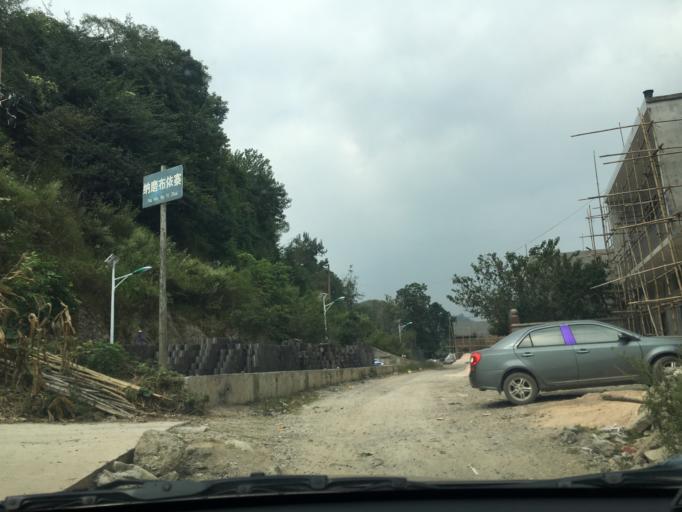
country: CN
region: Guizhou Sheng
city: Anshun
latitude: 25.5735
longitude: 105.6320
